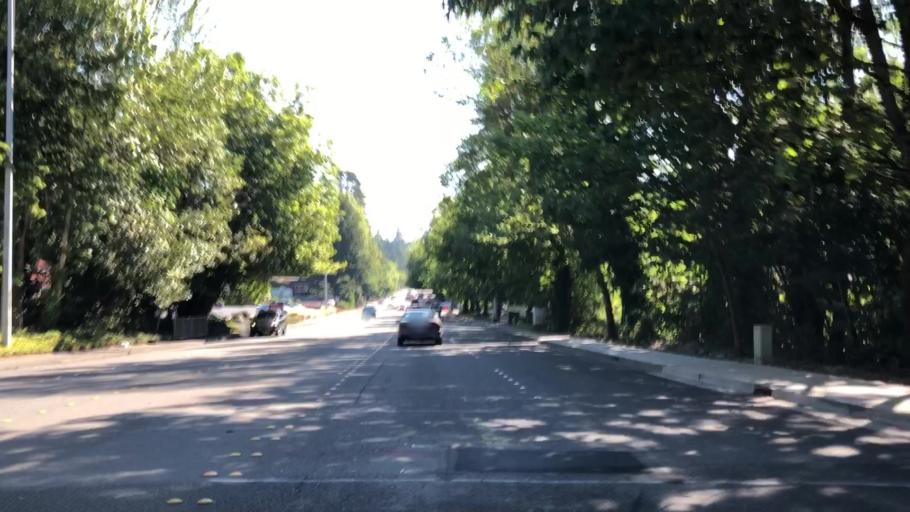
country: US
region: Washington
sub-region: King County
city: Bellevue
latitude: 47.6234
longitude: -122.1584
